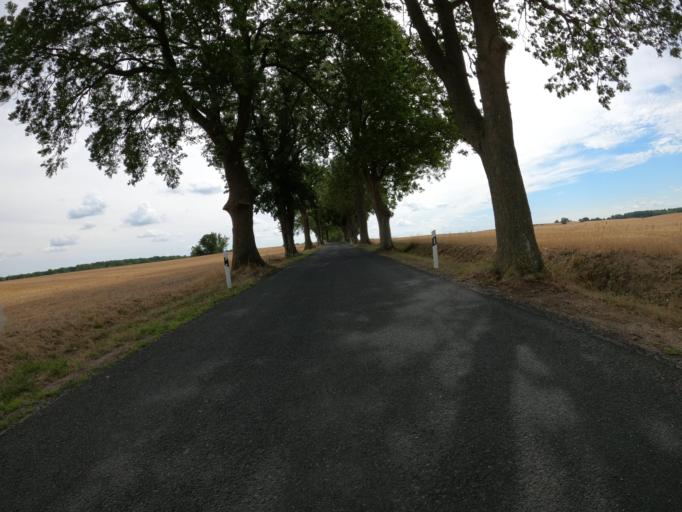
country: DE
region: Mecklenburg-Vorpommern
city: Loitz
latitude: 53.4136
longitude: 13.4337
